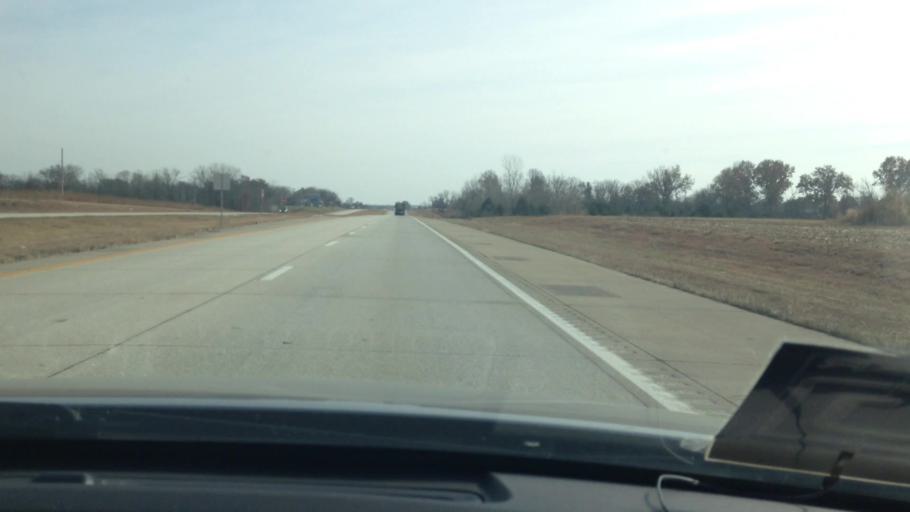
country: US
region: Missouri
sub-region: Henry County
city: Clinton
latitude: 38.4380
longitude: -93.9430
